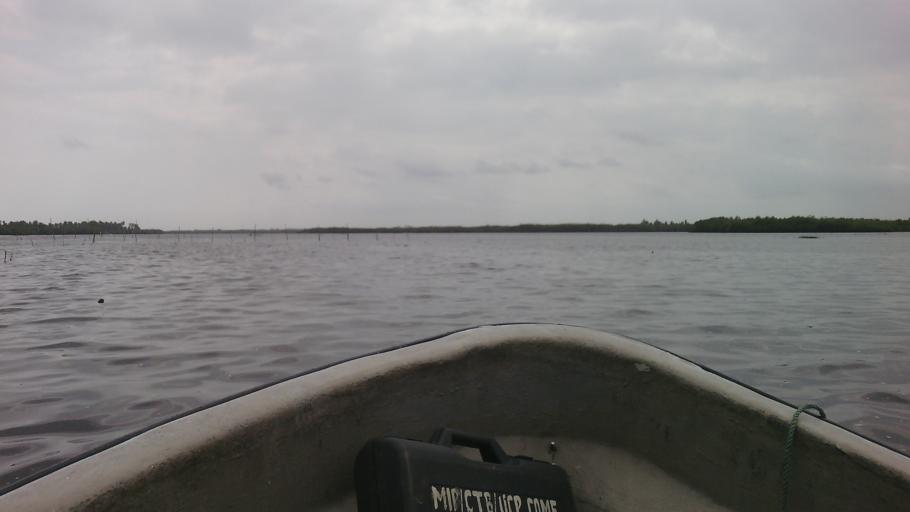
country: BJ
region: Atlantique
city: Ouidah
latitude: 6.3080
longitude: 1.9778
